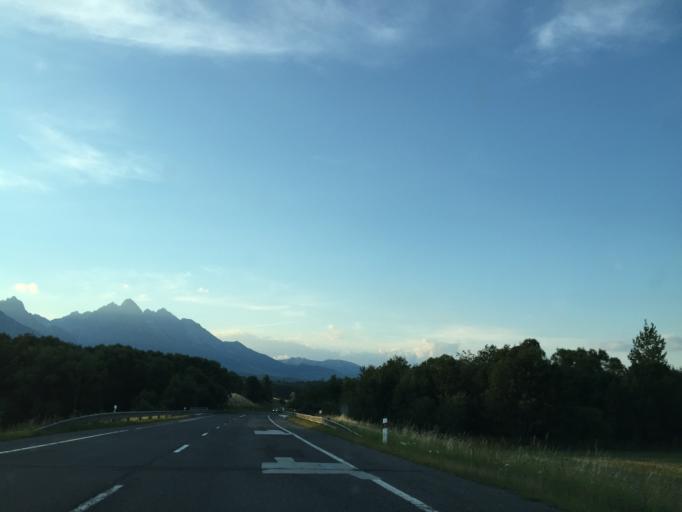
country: SK
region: Presovsky
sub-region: Okres Poprad
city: Nova Lesna
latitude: 49.1018
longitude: 20.2599
